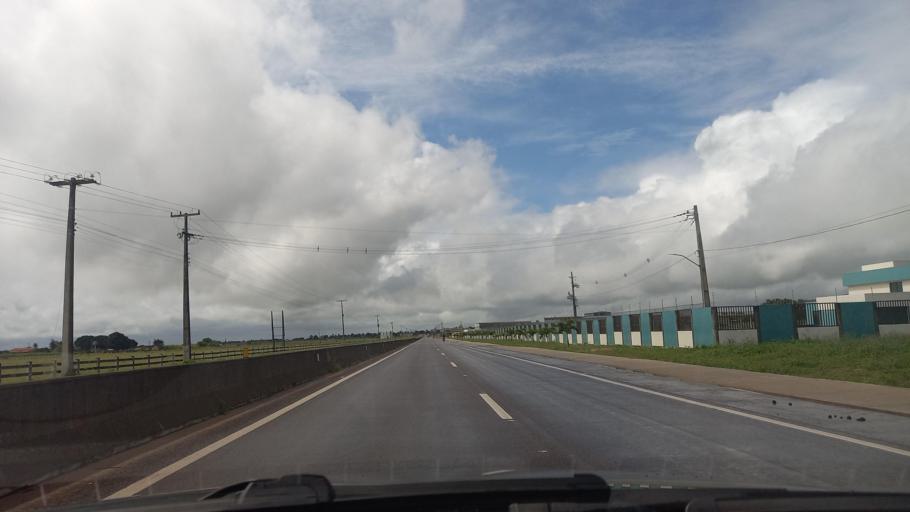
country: BR
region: Alagoas
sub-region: Limoeiro De Anadia
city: Limoeiro de Anadia
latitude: -9.7594
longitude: -36.5486
